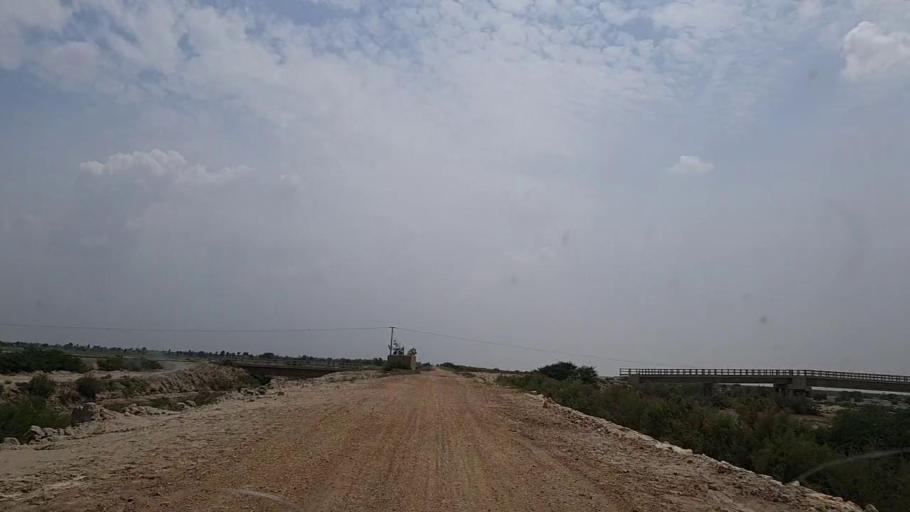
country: PK
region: Sindh
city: Phulji
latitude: 26.8220
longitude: 67.6128
